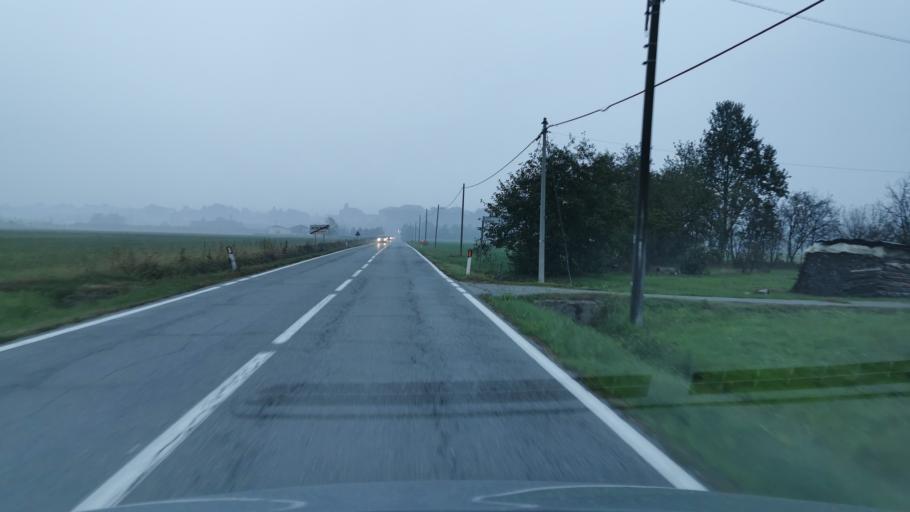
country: IT
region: Piedmont
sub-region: Provincia di Torino
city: Aglie
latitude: 45.3509
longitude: 7.7668
